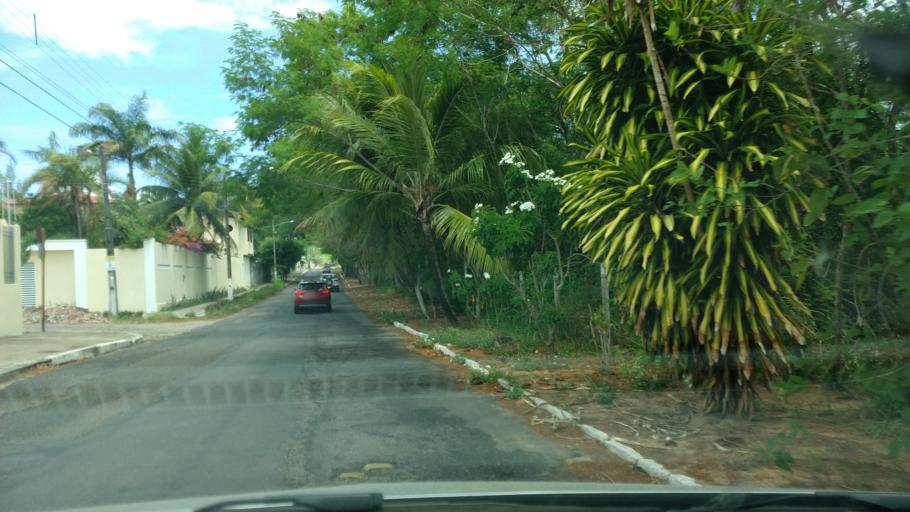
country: BR
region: Rio Grande do Norte
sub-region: Natal
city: Natal
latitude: -5.8478
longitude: -35.1973
